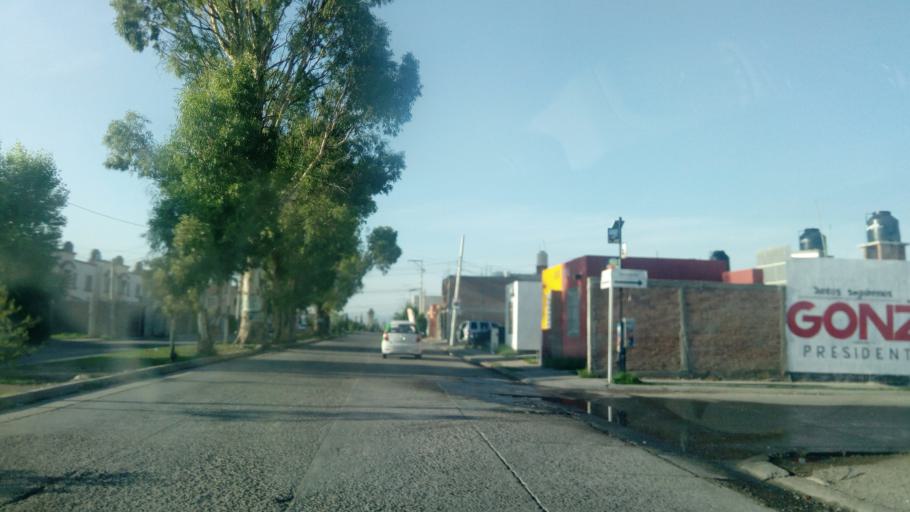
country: MX
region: Durango
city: Victoria de Durango
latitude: 24.0742
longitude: -104.5877
